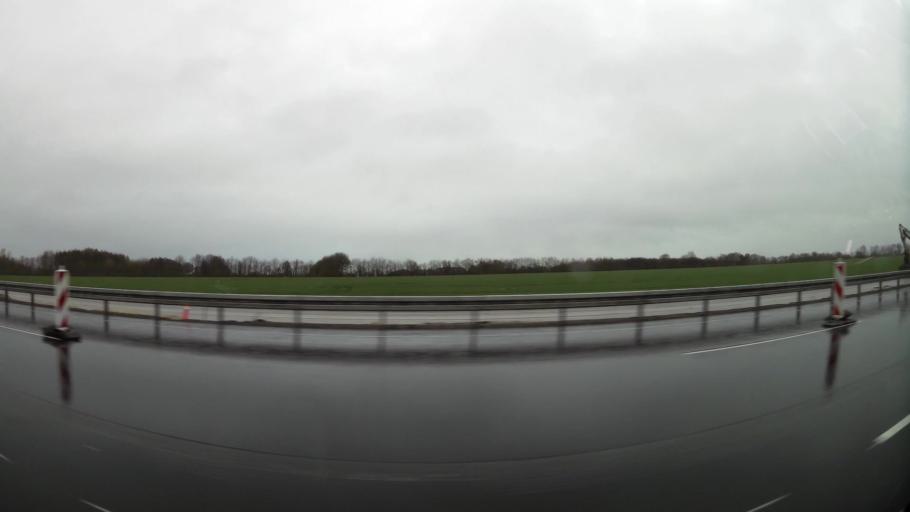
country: DK
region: Central Jutland
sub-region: Herning Kommune
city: Snejbjerg
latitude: 56.2130
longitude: 8.8609
